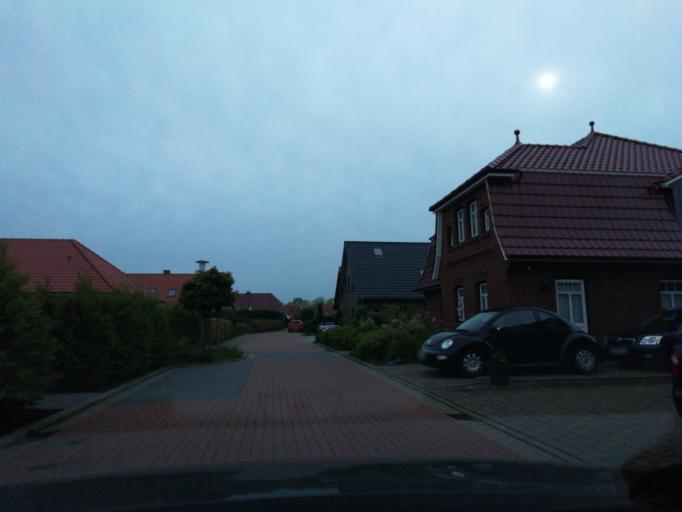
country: DE
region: Lower Saxony
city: Schillig
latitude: 53.6326
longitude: 8.0306
